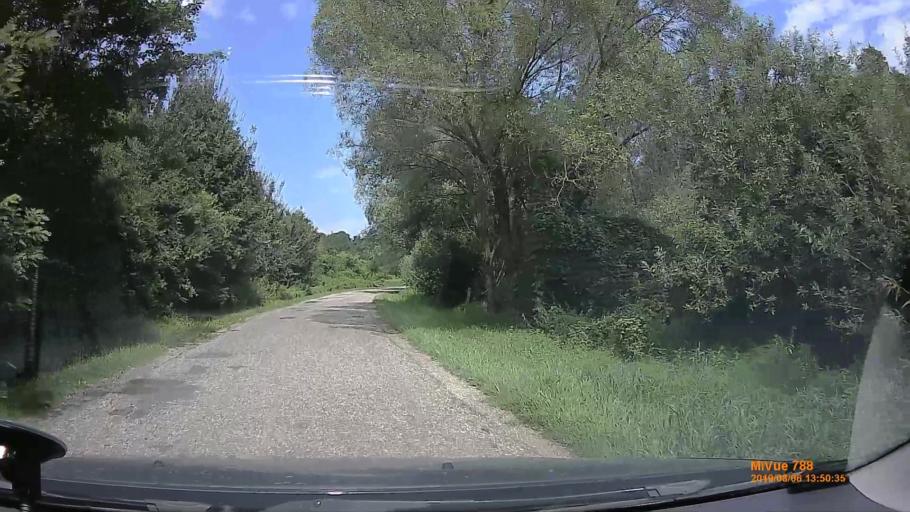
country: HU
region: Zala
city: Zalakomar
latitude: 46.5742
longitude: 17.1103
